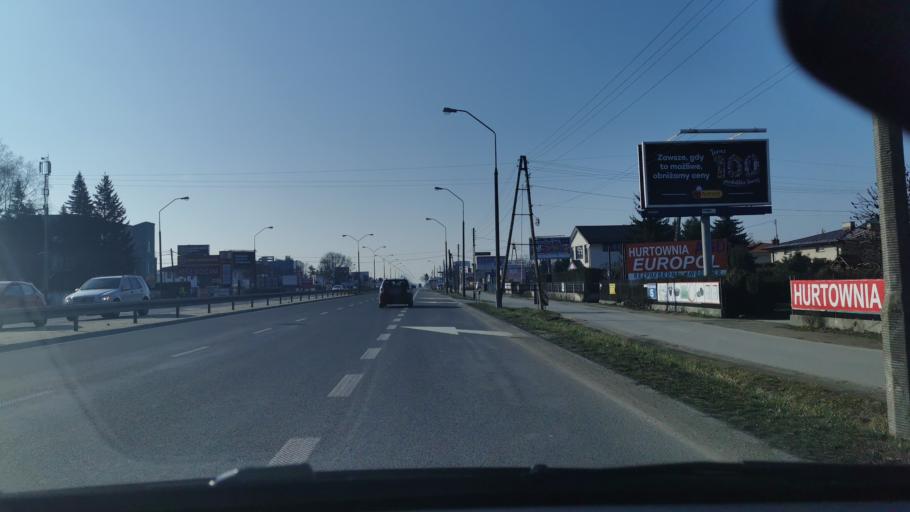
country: PL
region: Masovian Voivodeship
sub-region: Powiat pruszkowski
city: Nowe Grocholice
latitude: 52.1316
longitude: 20.8976
